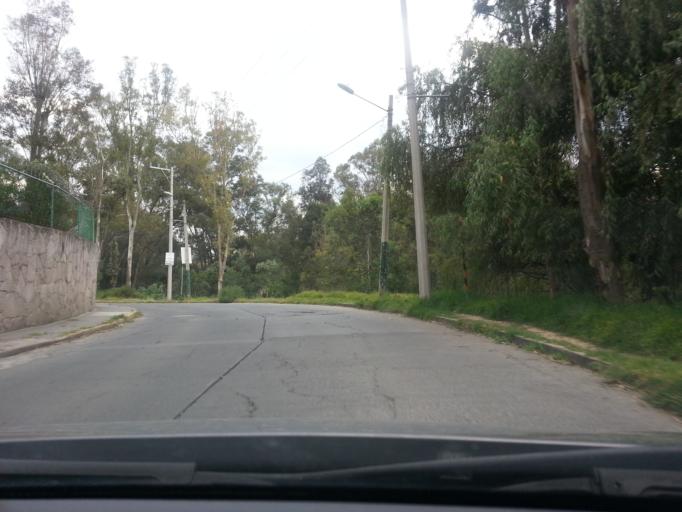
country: MX
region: Mexico
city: Cuautitlan Izcalli
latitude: 19.6218
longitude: -99.2411
